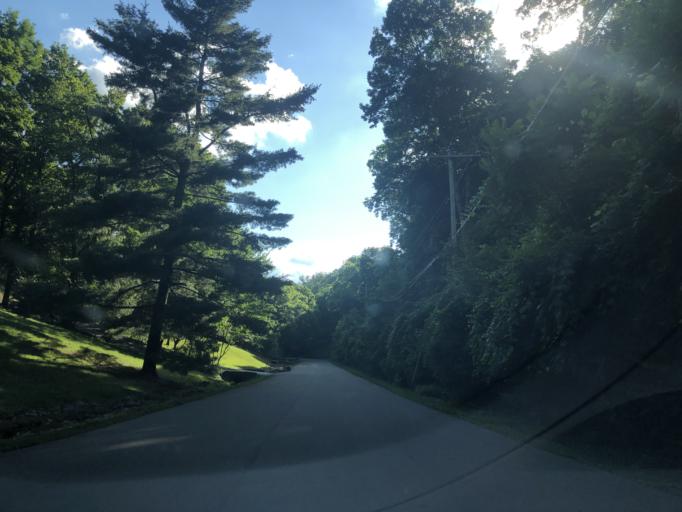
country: US
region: Tennessee
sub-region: Davidson County
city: Forest Hills
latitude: 36.0707
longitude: -86.8200
